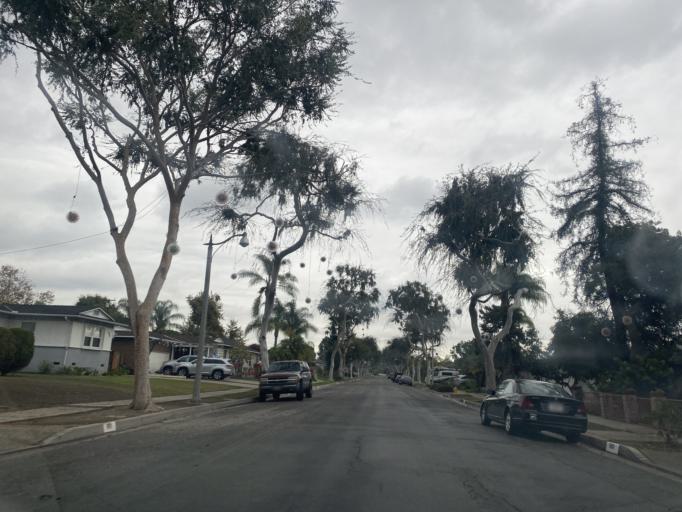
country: US
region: California
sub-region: Orange County
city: Fullerton
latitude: 33.8785
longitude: -117.9111
